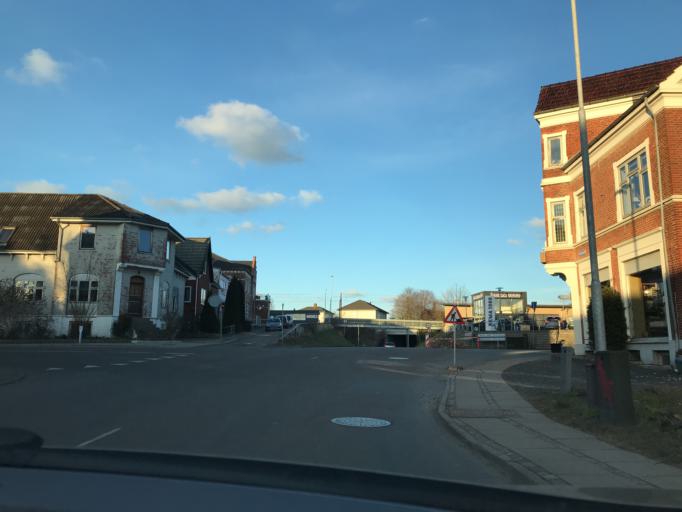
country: DK
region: South Denmark
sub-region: Middelfart Kommune
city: Norre Aby
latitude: 55.4586
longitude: 9.8711
